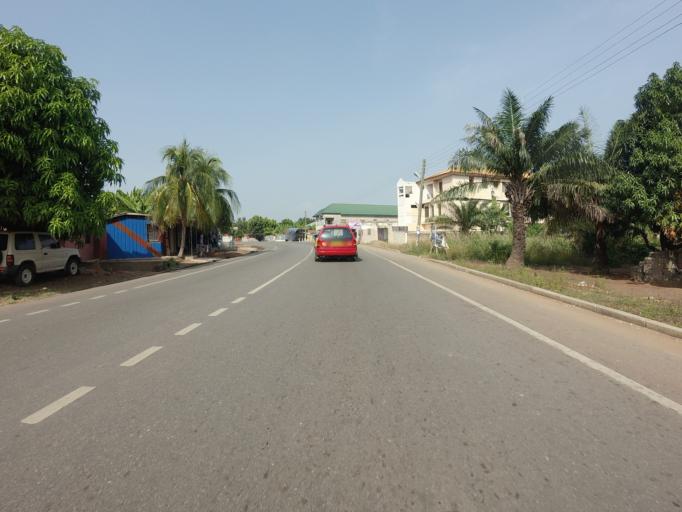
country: GH
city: Akropong
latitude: 6.1165
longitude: -0.0039
